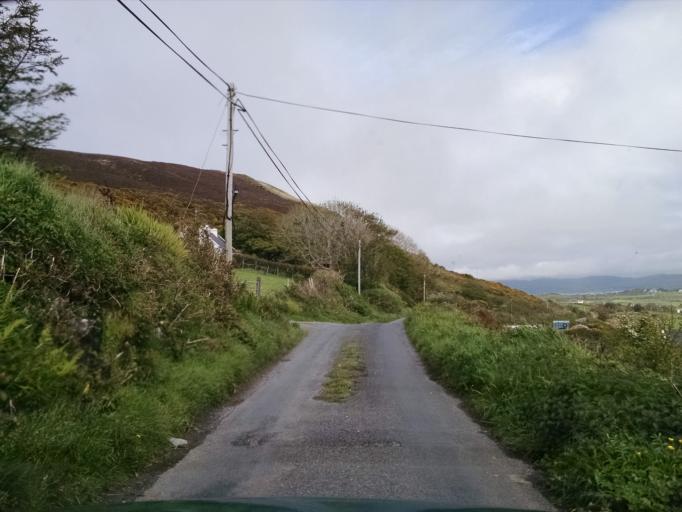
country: IE
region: Connaught
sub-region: County Galway
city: Clifden
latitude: 53.7612
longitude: -9.8540
